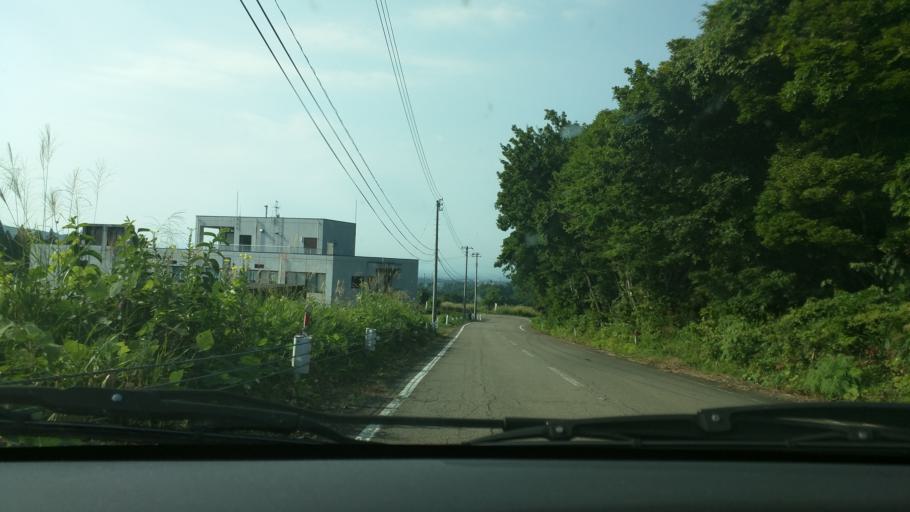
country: JP
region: Fukushima
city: Kitakata
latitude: 37.7341
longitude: 139.8707
